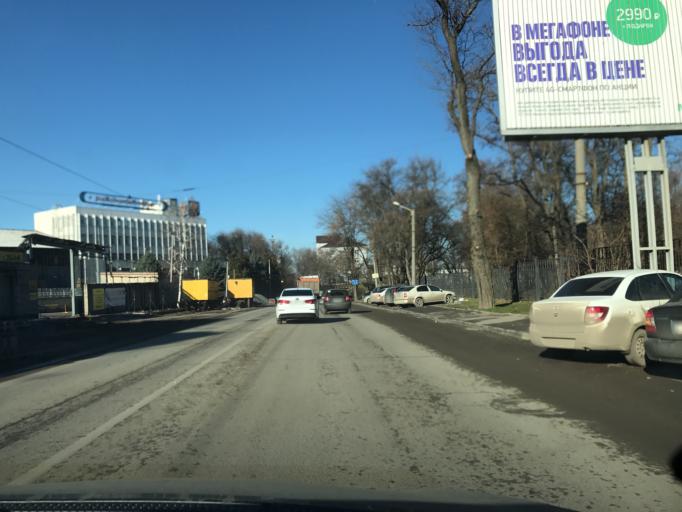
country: RU
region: Rostov
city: Rostov-na-Donu
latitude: 47.2420
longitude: 39.7520
